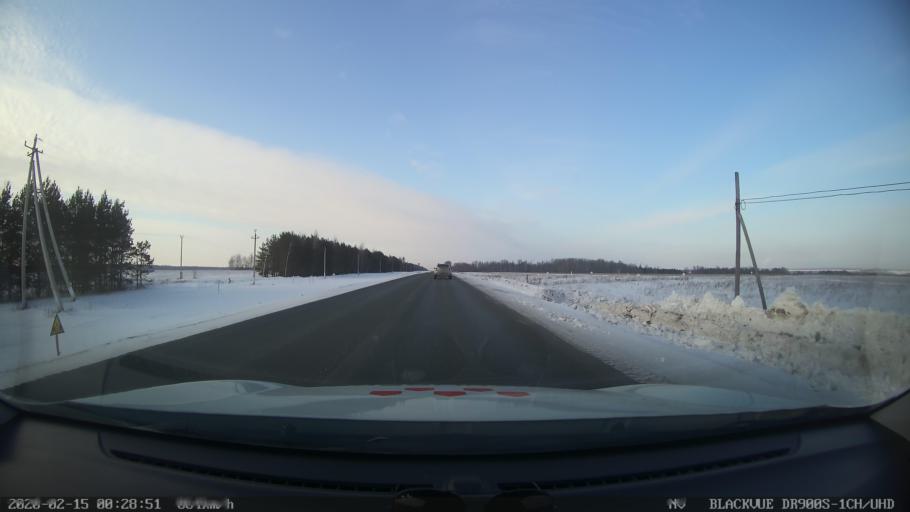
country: RU
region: Tatarstan
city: Verkhniy Uslon
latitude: 55.6460
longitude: 48.8734
